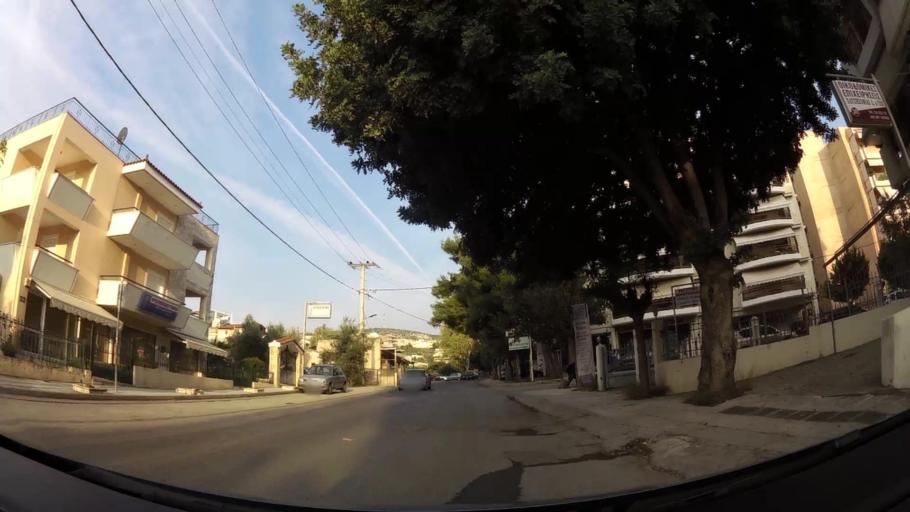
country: GR
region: Attica
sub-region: Nomarchia Athinas
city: Kamateron
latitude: 38.0571
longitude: 23.7102
